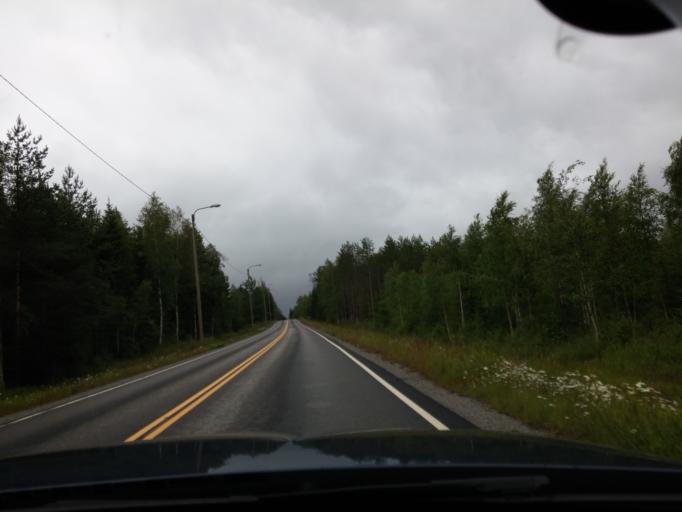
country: FI
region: Central Finland
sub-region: Saarijaervi-Viitasaari
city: Pylkoenmaeki
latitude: 62.6452
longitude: 24.9224
